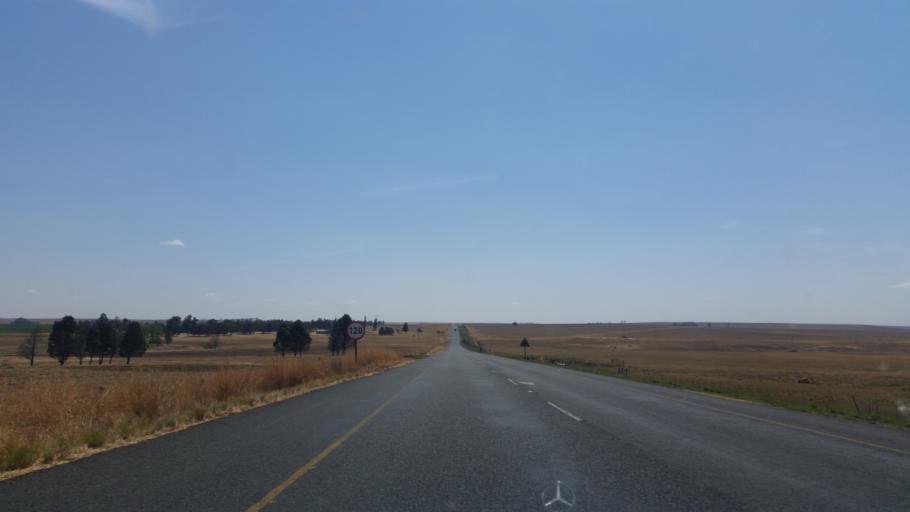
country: ZA
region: Orange Free State
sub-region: Thabo Mofutsanyana District Municipality
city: Phuthaditjhaba
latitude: -28.1983
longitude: 28.6875
